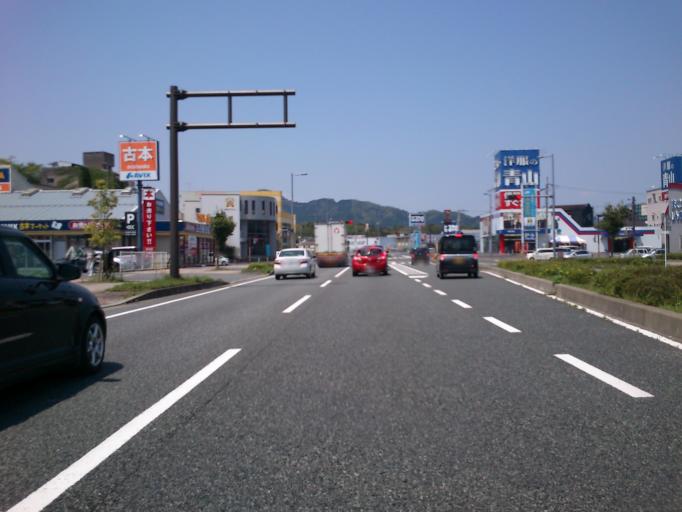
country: JP
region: Kyoto
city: Fukuchiyama
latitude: 35.2948
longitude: 135.1147
